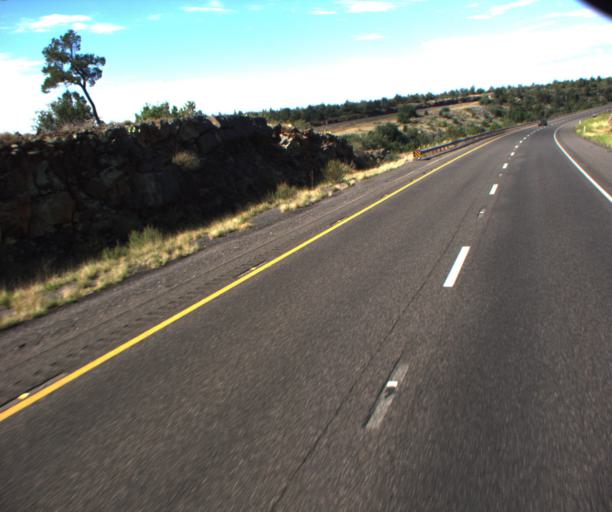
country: US
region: Arizona
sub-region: Yavapai County
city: Village of Oak Creek (Big Park)
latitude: 34.7717
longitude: -111.6403
